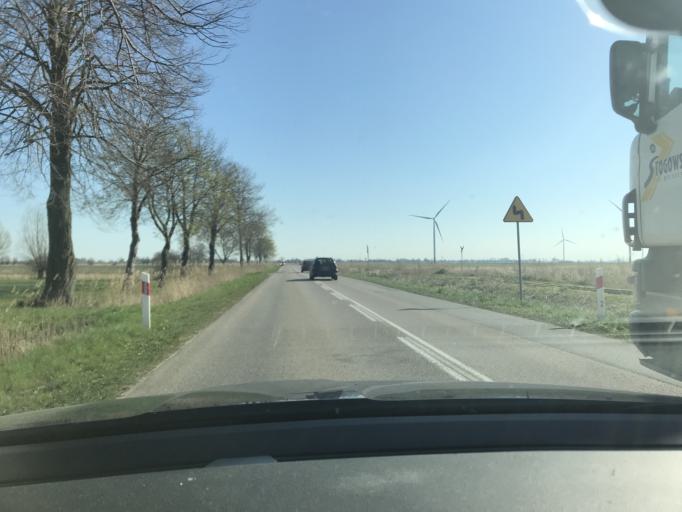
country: PL
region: Pomeranian Voivodeship
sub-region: Powiat nowodworski
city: Nowy Dwor Gdanski
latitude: 54.2607
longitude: 19.1364
